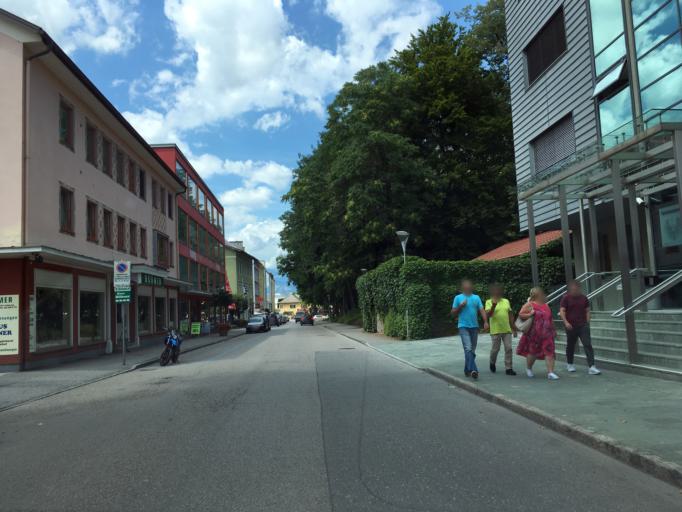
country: AT
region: Carinthia
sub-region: Politischer Bezirk Spittal an der Drau
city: Spittal an der Drau
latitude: 46.7969
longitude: 13.4946
